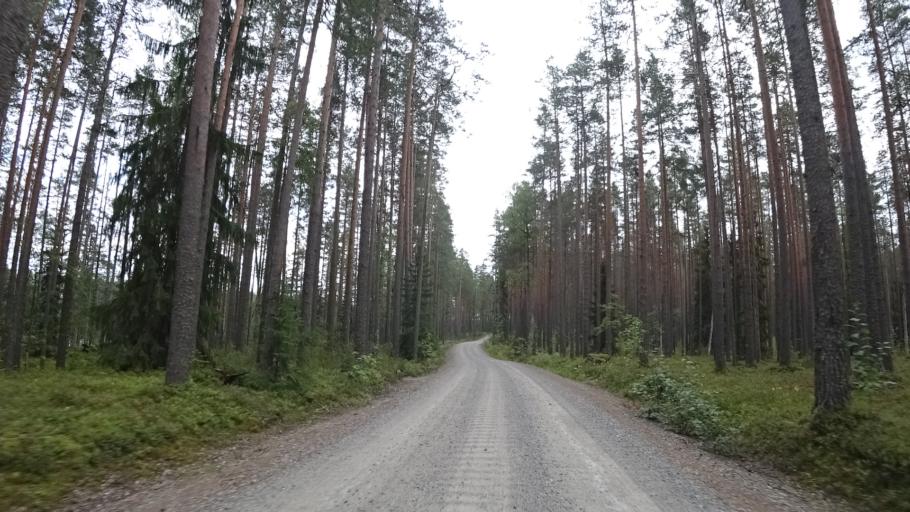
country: FI
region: North Karelia
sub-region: Joensuu
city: Ilomantsi
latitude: 62.5933
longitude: 31.1814
